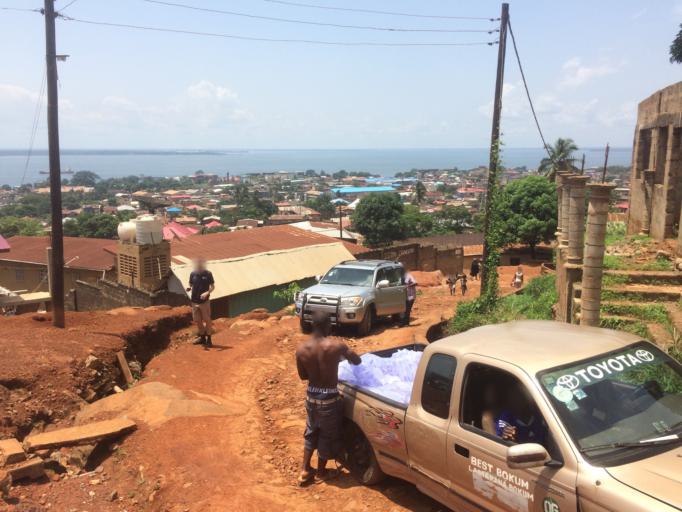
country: SL
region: Western Area
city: Freetown
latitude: 8.4705
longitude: -13.1990
